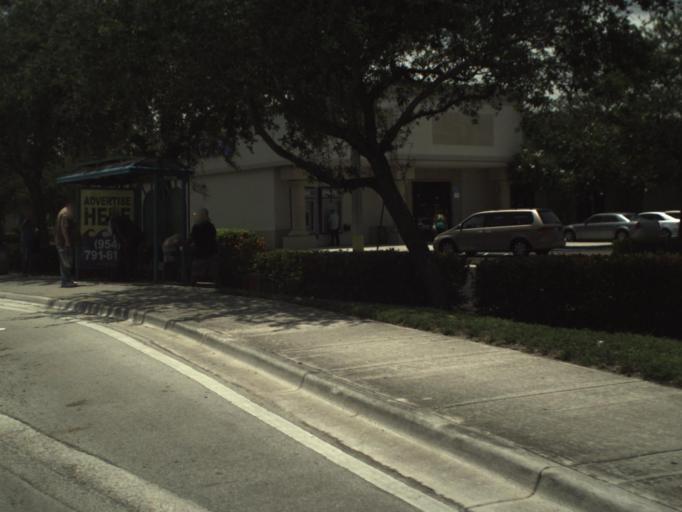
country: US
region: Florida
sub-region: Broward County
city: Coconut Creek
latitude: 26.2295
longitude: -80.1568
